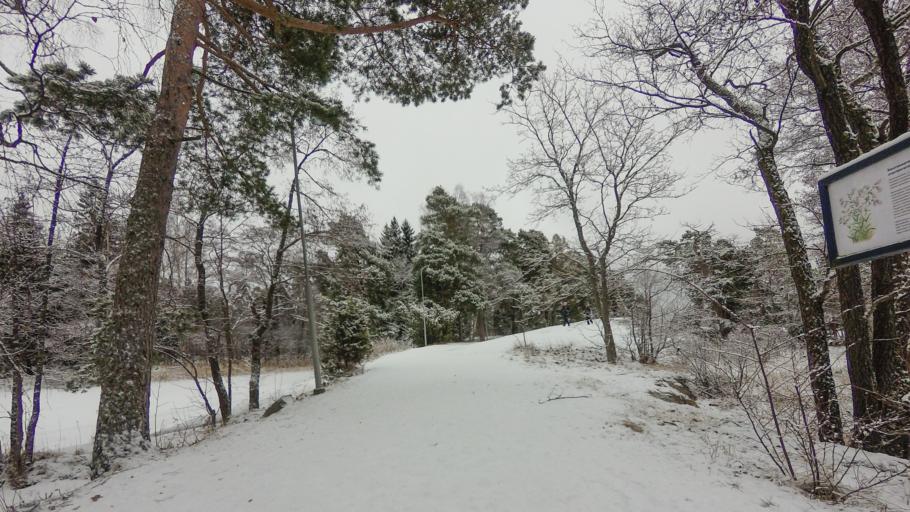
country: FI
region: Uusimaa
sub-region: Helsinki
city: Teekkarikylae
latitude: 60.1766
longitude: 24.8845
